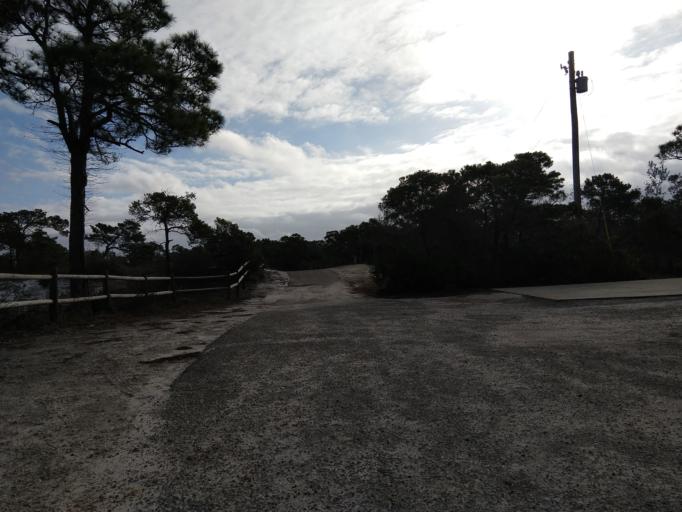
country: US
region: Florida
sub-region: Gulf County
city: Port Saint Joe
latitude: 29.7889
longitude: -85.4074
